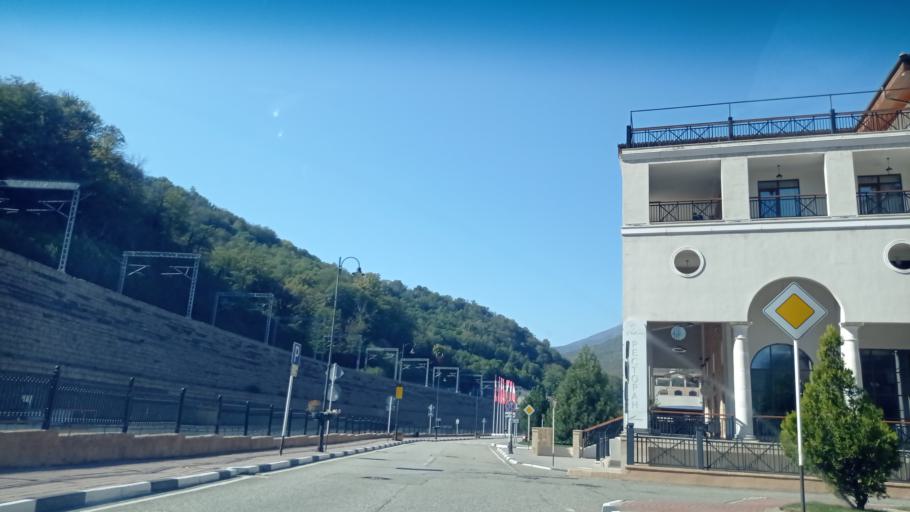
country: RU
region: Krasnodarskiy
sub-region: Sochi City
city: Krasnaya Polyana
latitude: 43.6827
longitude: 40.2582
